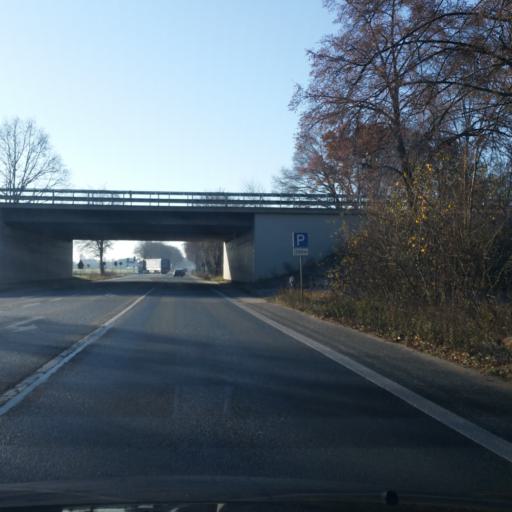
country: DE
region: North Rhine-Westphalia
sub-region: Regierungsbezirk Munster
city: Isselburg
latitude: 51.8176
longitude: 6.4418
